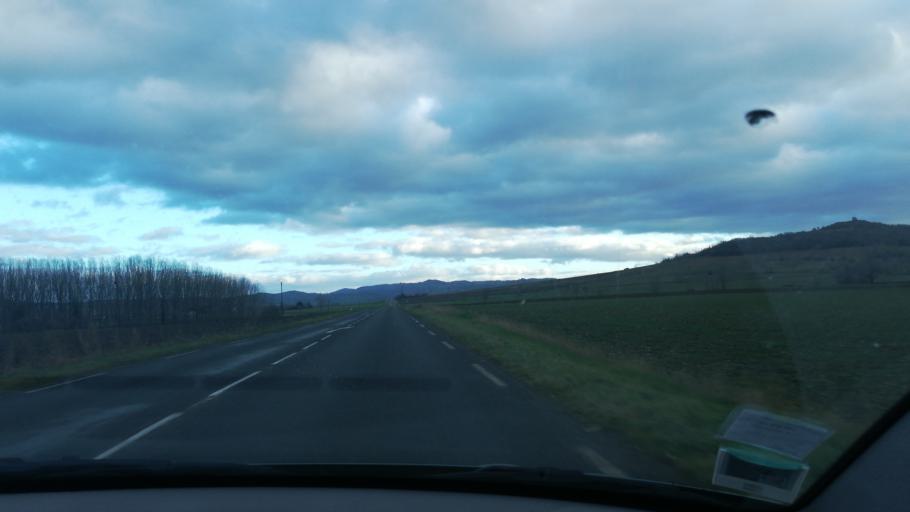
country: FR
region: Auvergne
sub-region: Departement du Puy-de-Dome
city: Vertaizon
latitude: 45.7572
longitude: 3.3133
